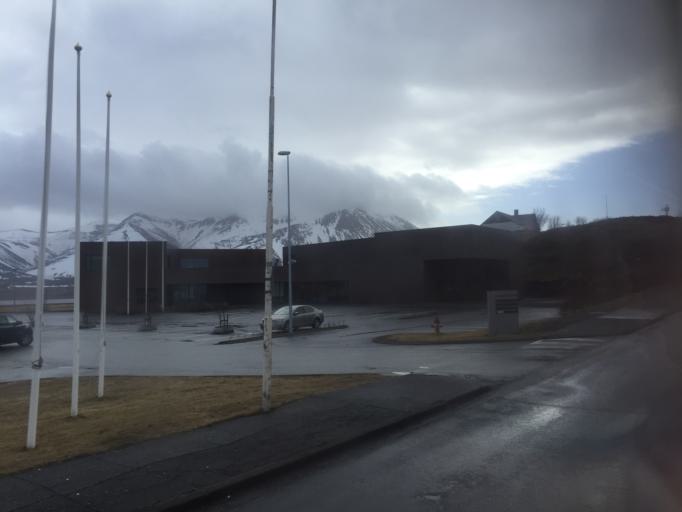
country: IS
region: West
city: Borgarnes
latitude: 64.5429
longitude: -21.9132
